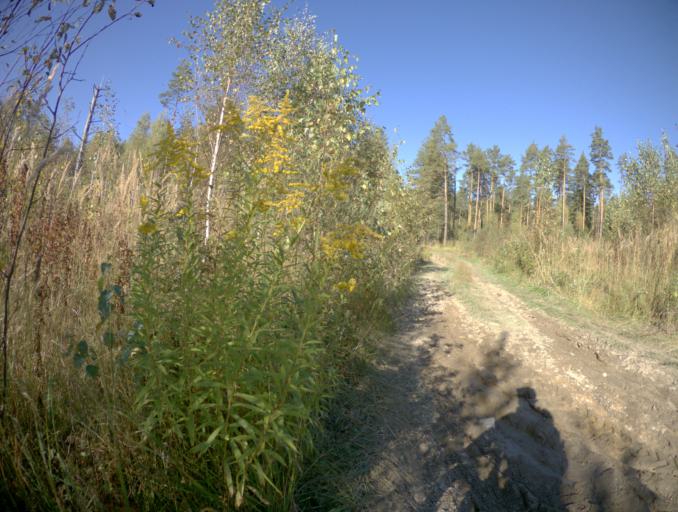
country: RU
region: Vladimir
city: Kameshkovo
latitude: 56.3629
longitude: 40.9640
